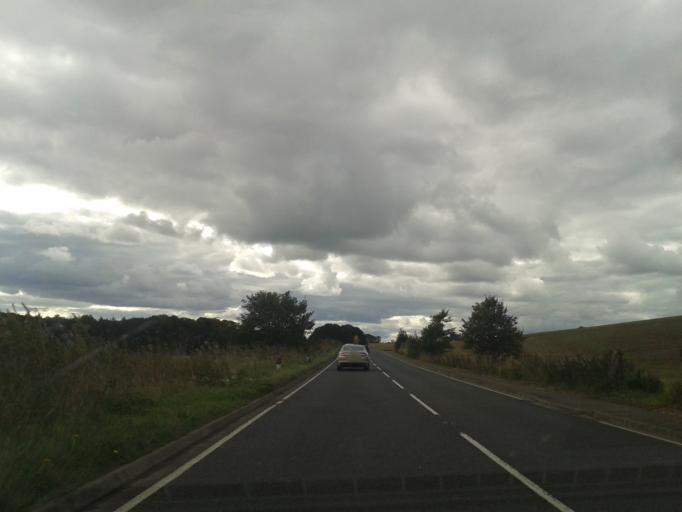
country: GB
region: Scotland
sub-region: Fife
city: Ceres
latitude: 56.3355
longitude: -2.9702
